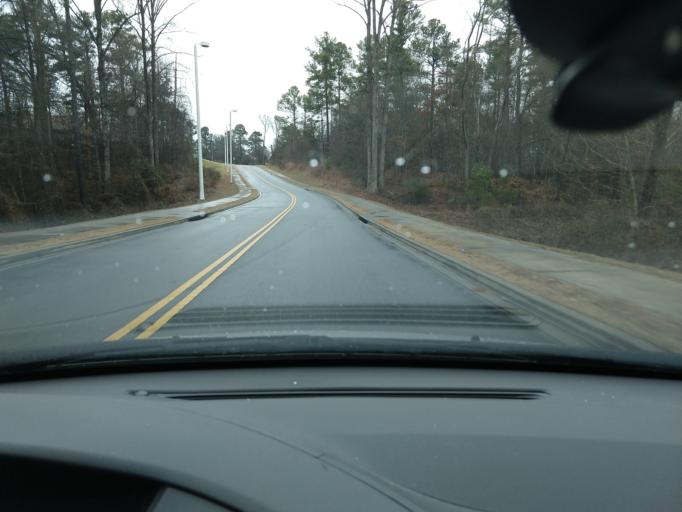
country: US
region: South Carolina
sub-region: Greenville County
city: Mauldin
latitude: 34.8124
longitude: -82.3320
